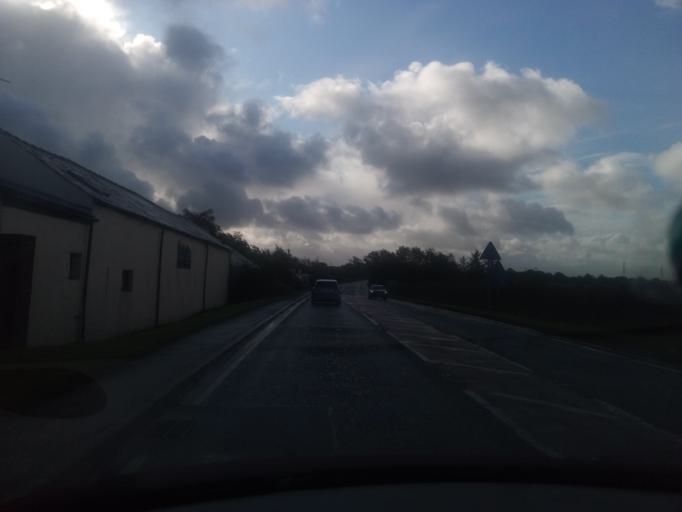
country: GB
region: England
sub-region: Cumbria
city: Carlisle
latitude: 54.9515
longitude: -2.9433
